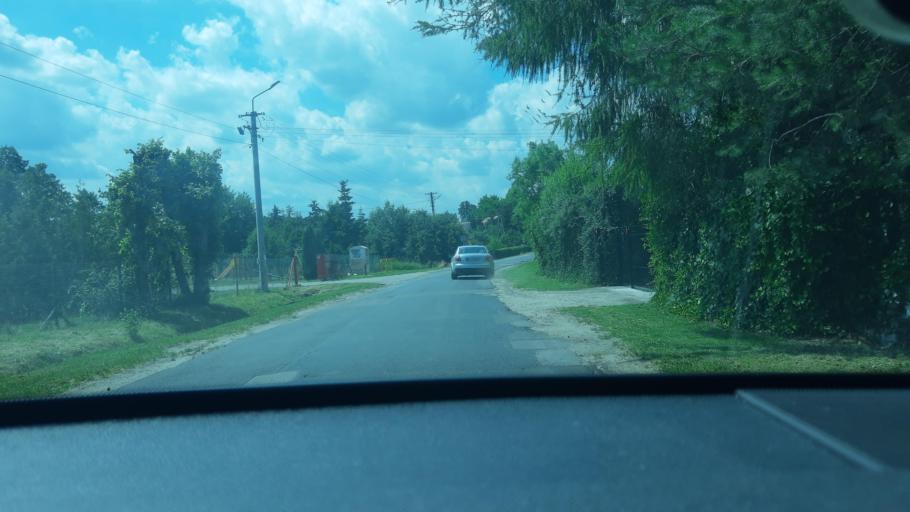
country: PL
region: Lodz Voivodeship
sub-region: Powiat sieradzki
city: Sieradz
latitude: 51.5482
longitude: 18.7565
